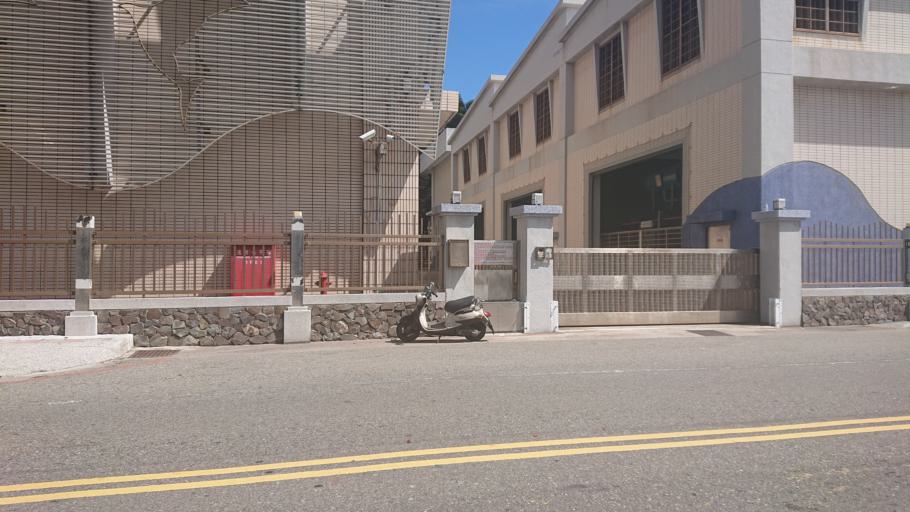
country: TW
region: Taiwan
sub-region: Penghu
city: Ma-kung
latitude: 23.5683
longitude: 119.5720
